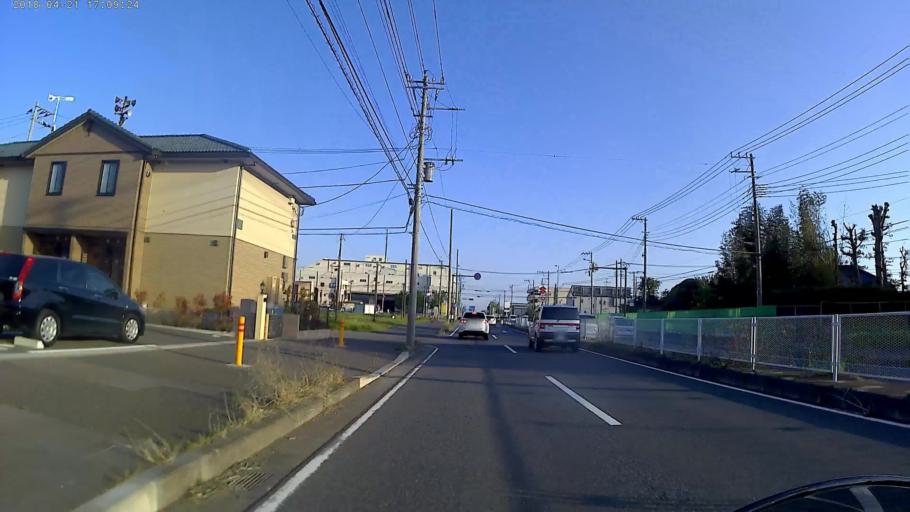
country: JP
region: Kanagawa
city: Fujisawa
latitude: 35.3973
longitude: 139.4429
